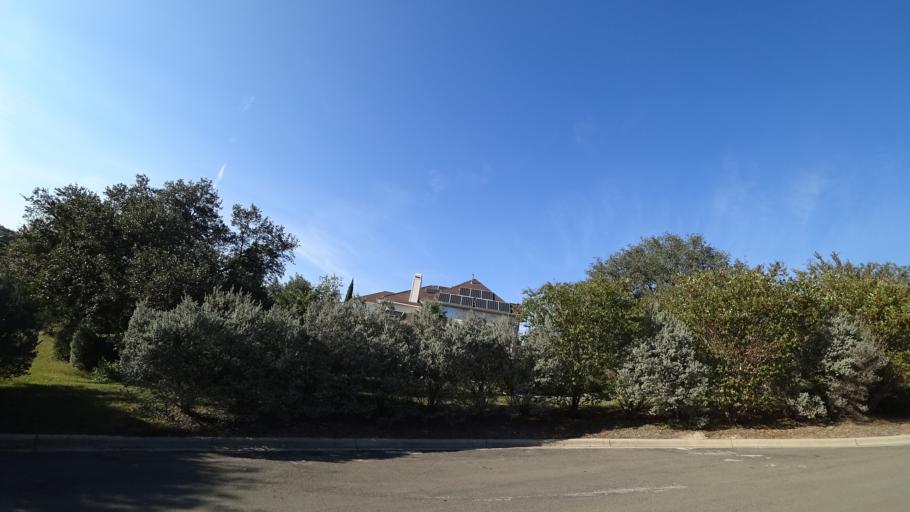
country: US
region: Texas
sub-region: Williamson County
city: Anderson Mill
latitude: 30.4353
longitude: -97.8126
